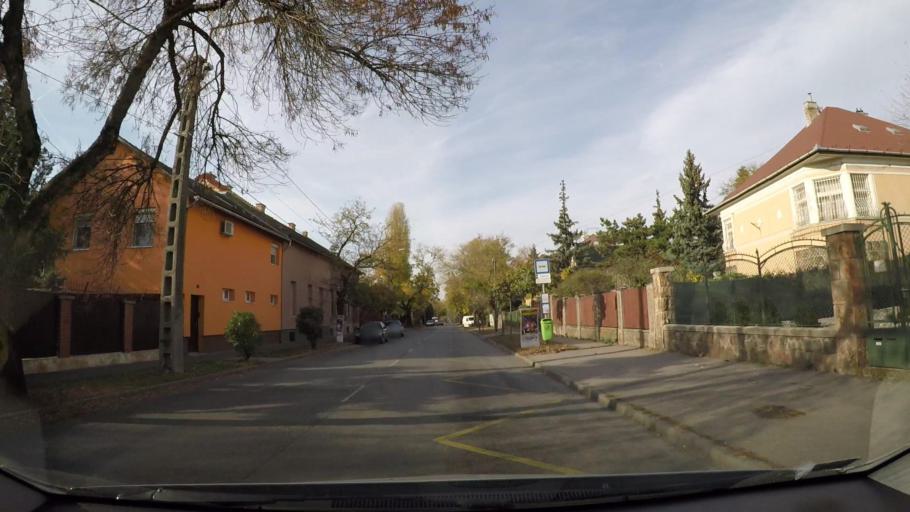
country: HU
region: Budapest
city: Budapest X. keruelet
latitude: 47.4774
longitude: 19.1449
